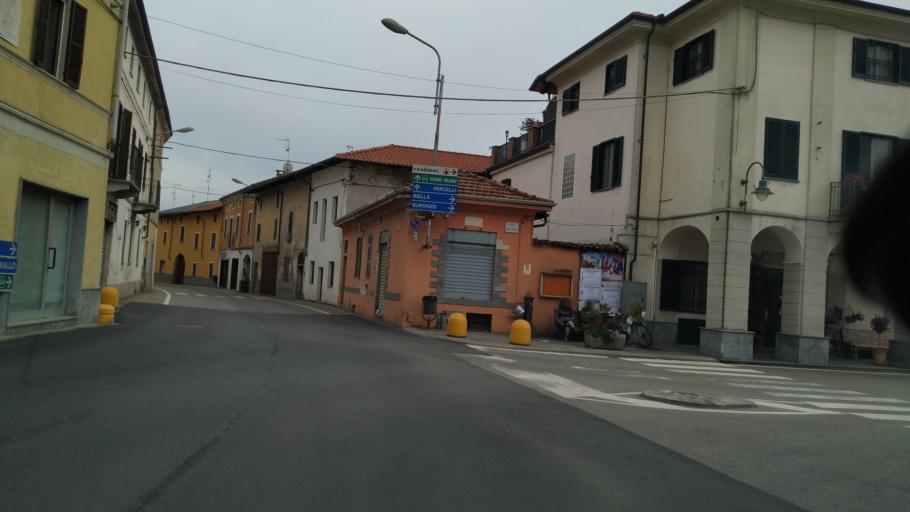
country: IT
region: Piedmont
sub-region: Provincia di Vercelli
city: Arborio
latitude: 45.4957
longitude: 8.3891
